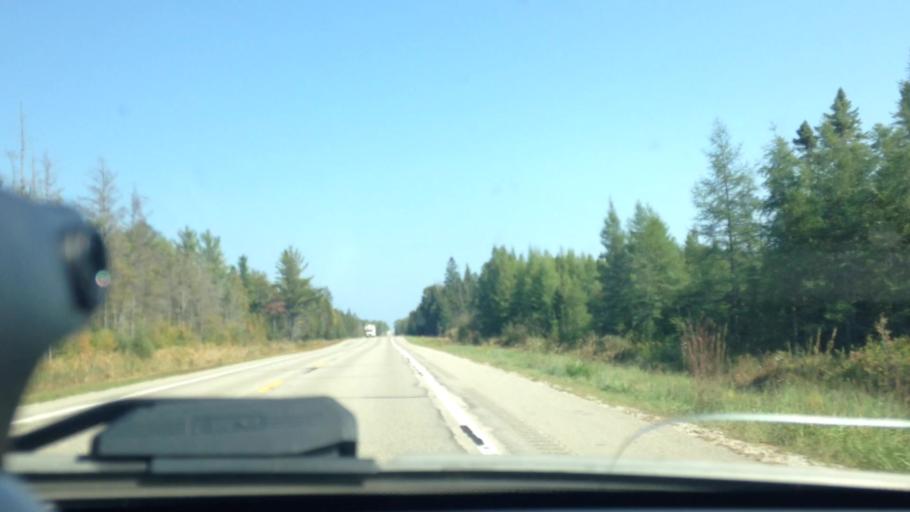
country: US
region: Michigan
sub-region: Luce County
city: Newberry
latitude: 46.3036
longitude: -85.3155
